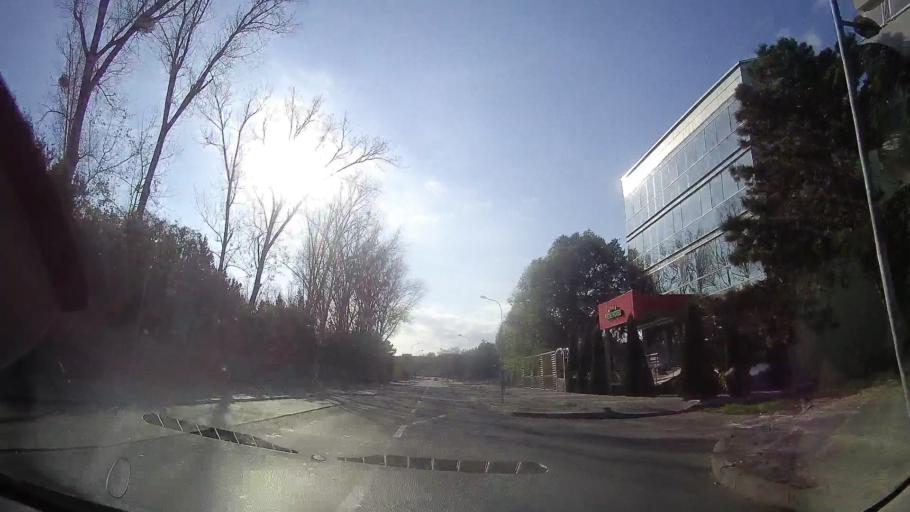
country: RO
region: Constanta
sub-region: Comuna Douazeci si Trei August
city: Douazeci si Trei August
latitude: 43.8734
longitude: 28.6016
